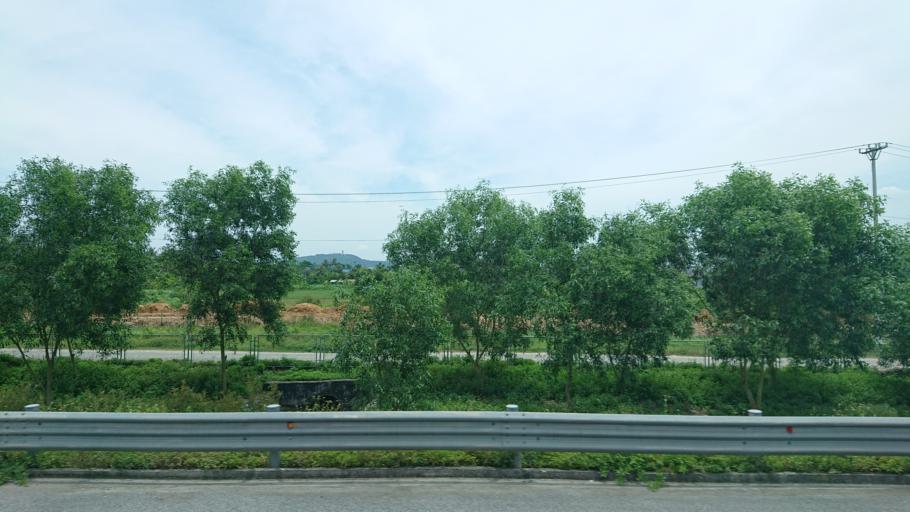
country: VN
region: Hai Phong
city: Nui Doi
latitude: 20.7690
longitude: 106.6304
